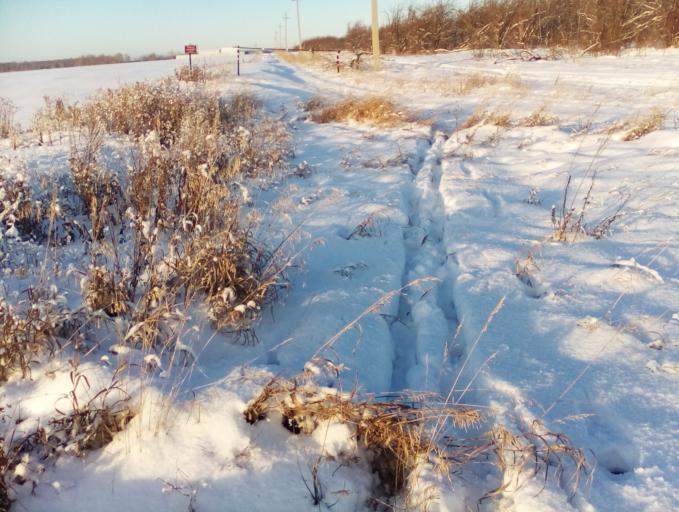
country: RU
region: Chelyabinsk
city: Poletayevo
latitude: 54.9810
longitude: 60.9479
